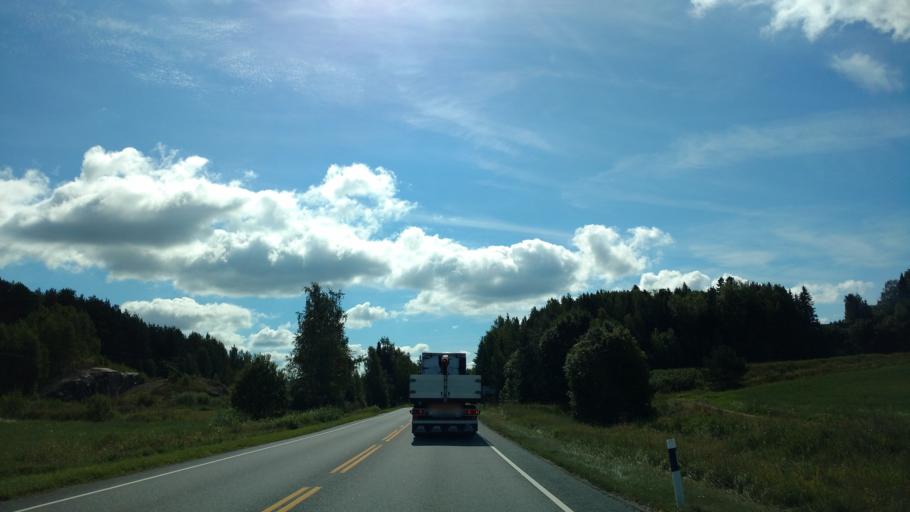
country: FI
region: Varsinais-Suomi
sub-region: Salo
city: Pernioe
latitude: 60.2765
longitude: 23.1226
